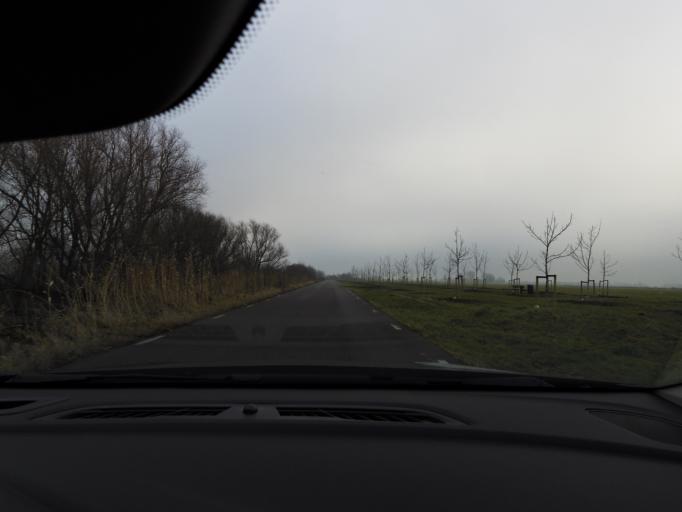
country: NL
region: South Holland
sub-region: Gemeente Oud-Beijerland
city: Oud-Beijerland
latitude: 51.8388
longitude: 4.3791
